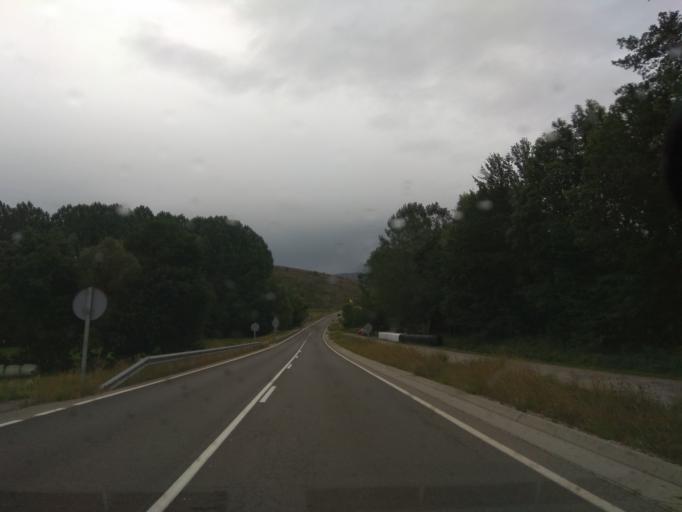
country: ES
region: Catalonia
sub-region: Provincia de Lleida
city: Bellver de Cerdanya
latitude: 42.3682
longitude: 1.7911
